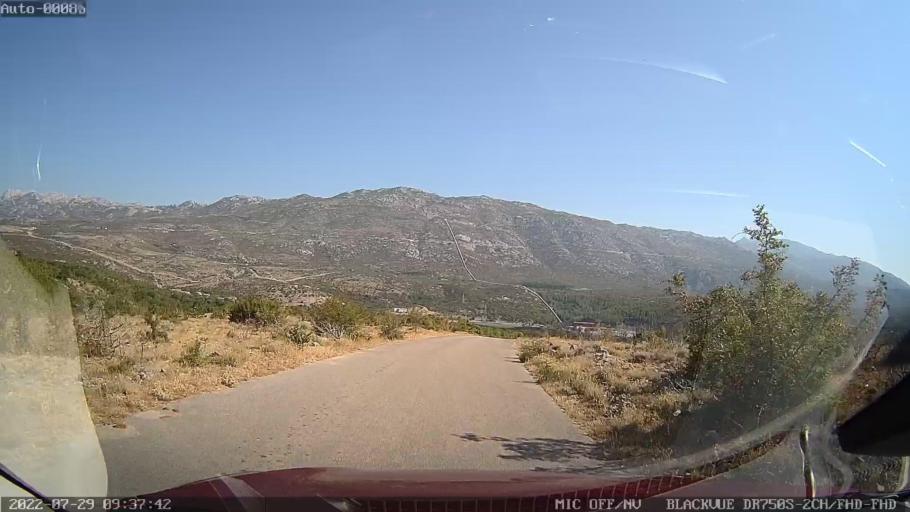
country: HR
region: Zadarska
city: Obrovac
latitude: 44.1980
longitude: 15.7467
